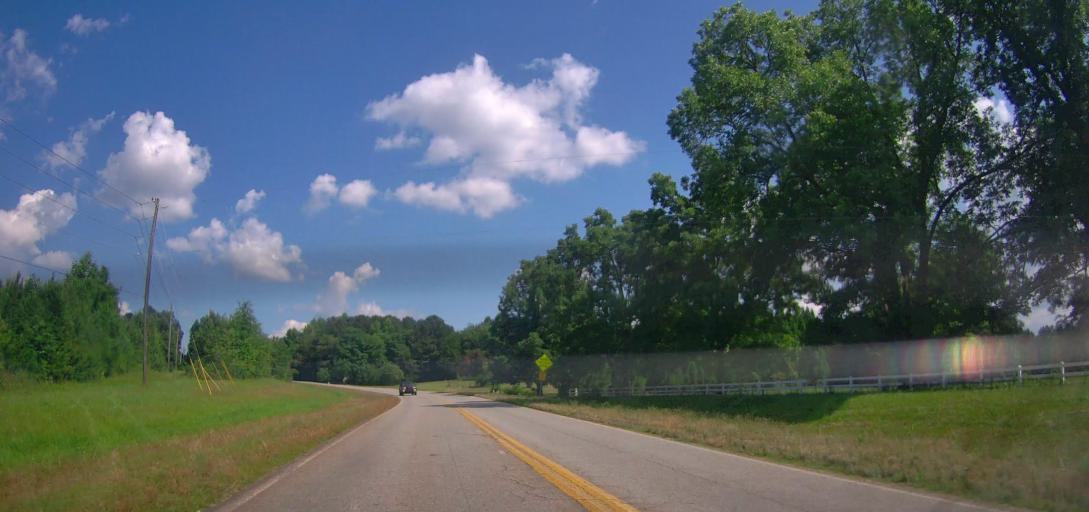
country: US
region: Georgia
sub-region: Spalding County
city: East Griffin
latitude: 33.2383
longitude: -84.1633
